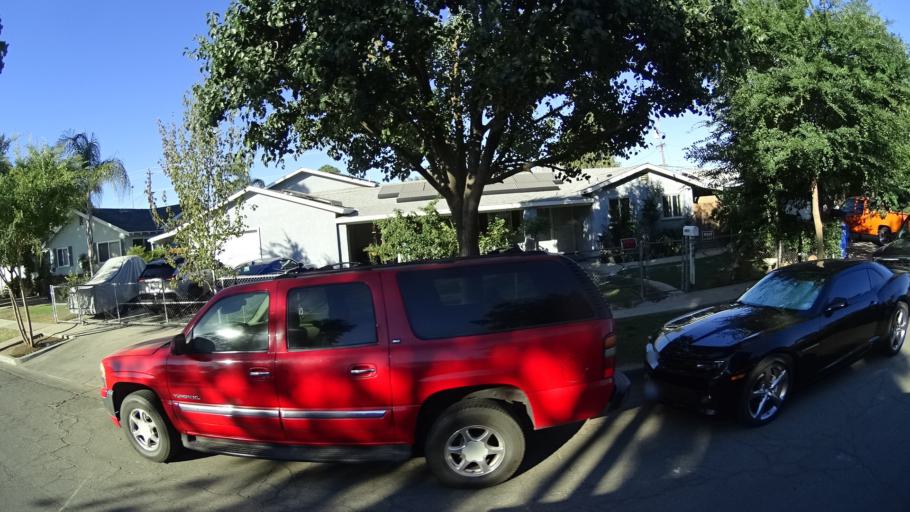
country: US
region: California
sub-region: Fresno County
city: Fresno
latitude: 36.7982
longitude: -119.8243
